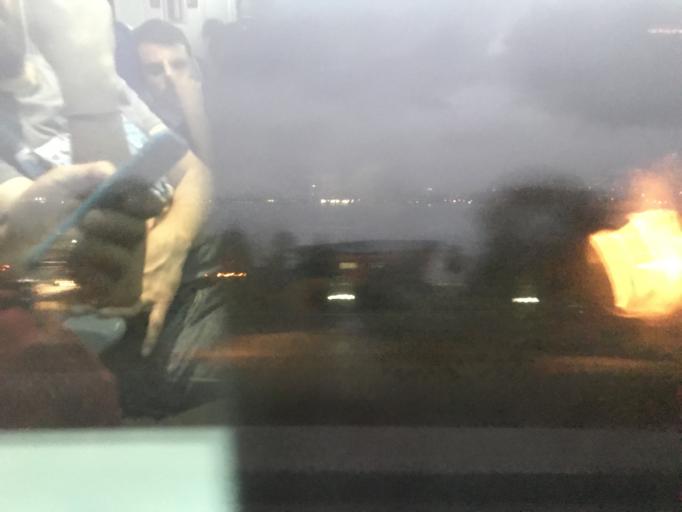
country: TR
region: Kocaeli
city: Derince
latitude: 40.7494
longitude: 29.8070
